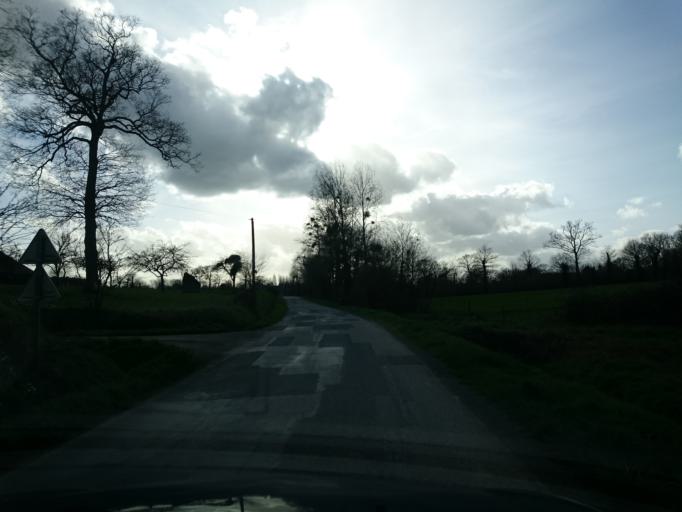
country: FR
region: Brittany
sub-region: Departement d'Ille-et-Vilaine
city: Chanteloup
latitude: 47.9261
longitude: -1.6215
